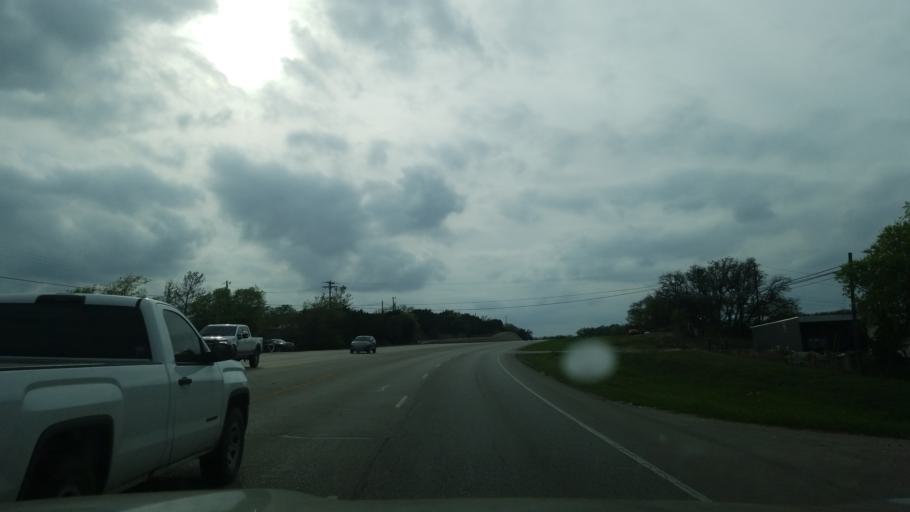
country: US
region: Texas
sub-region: Hays County
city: Dripping Springs
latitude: 30.2059
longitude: -98.1354
